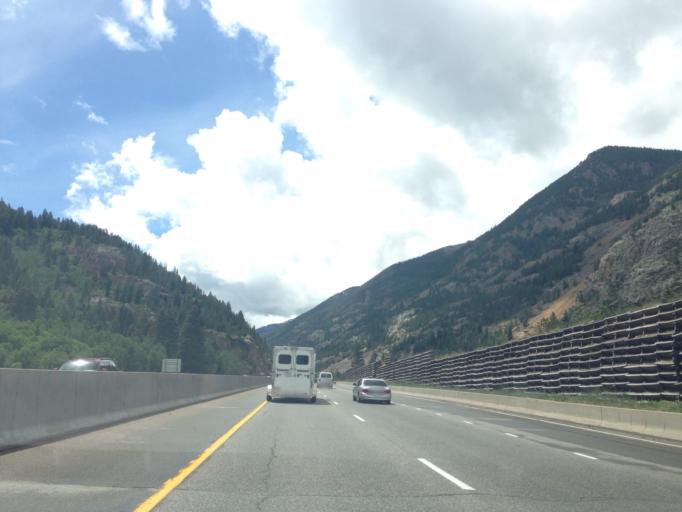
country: US
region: Colorado
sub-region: Clear Creek County
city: Georgetown
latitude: 39.6943
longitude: -105.7300
